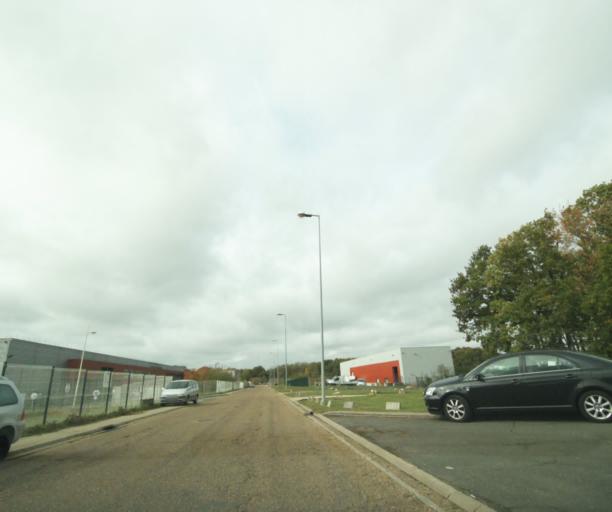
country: FR
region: Centre
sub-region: Departement d'Eure-et-Loir
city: Garnay
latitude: 48.7405
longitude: 1.3311
